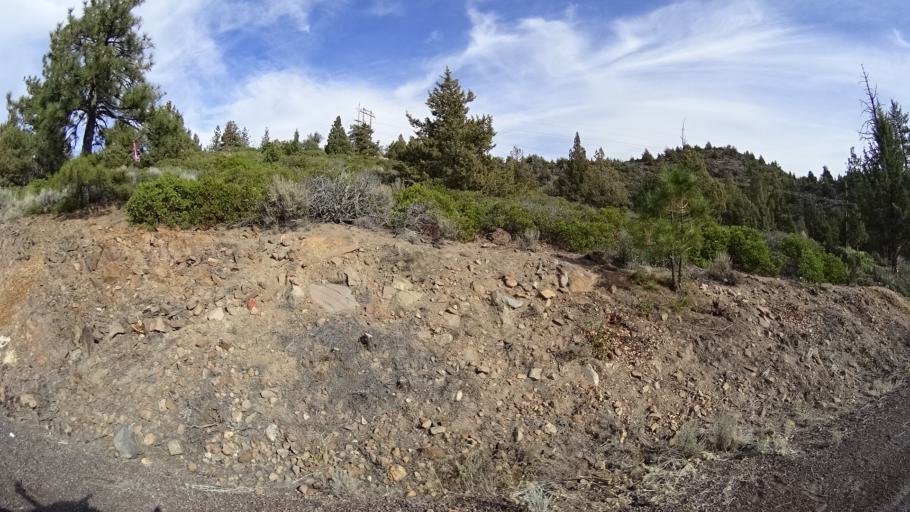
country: US
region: California
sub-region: Siskiyou County
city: Weed
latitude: 41.5148
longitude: -122.3655
